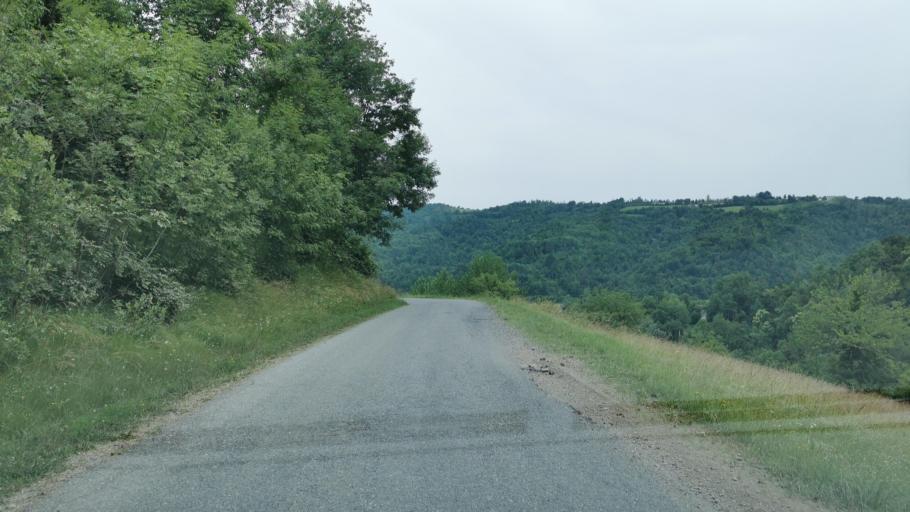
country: IT
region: Piedmont
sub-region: Provincia di Cuneo
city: Torresina
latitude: 44.4293
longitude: 8.0534
